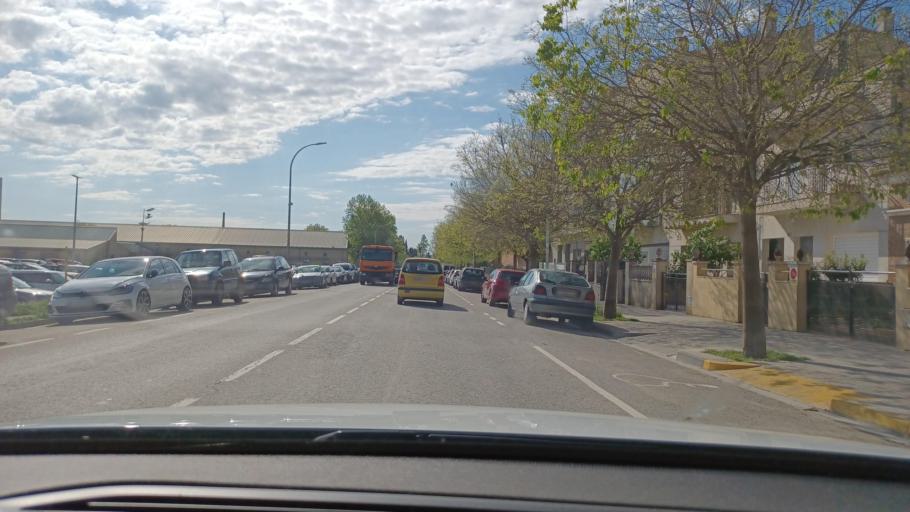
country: ES
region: Catalonia
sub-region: Provincia de Barcelona
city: Vilafranca del Penedes
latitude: 41.3565
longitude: 1.7024
